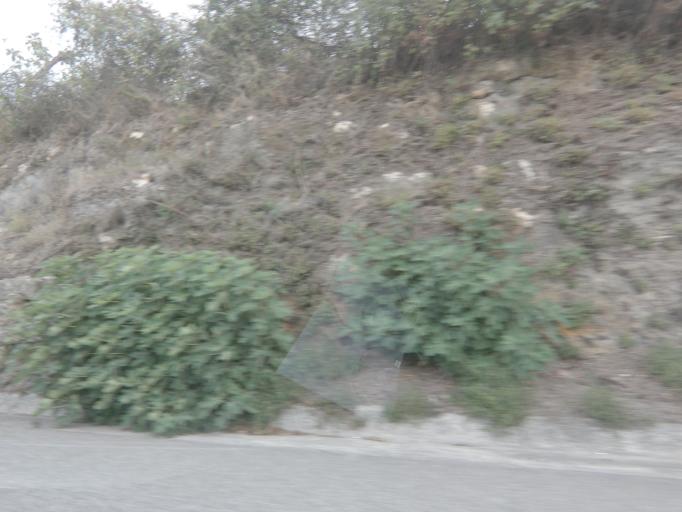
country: PT
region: Coimbra
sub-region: Condeixa-A-Nova
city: Condeixa-a-Nova
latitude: 40.1329
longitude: -8.4743
